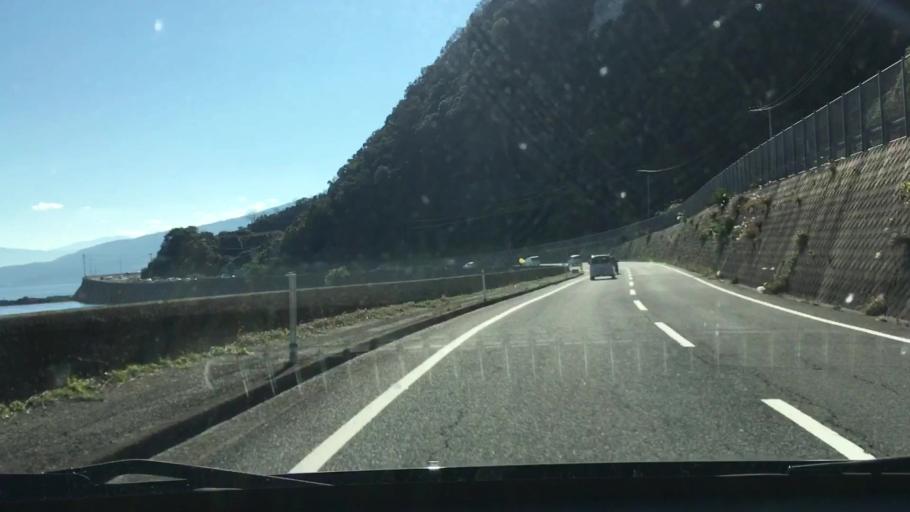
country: JP
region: Kagoshima
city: Kajiki
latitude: 31.6620
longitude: 130.6153
